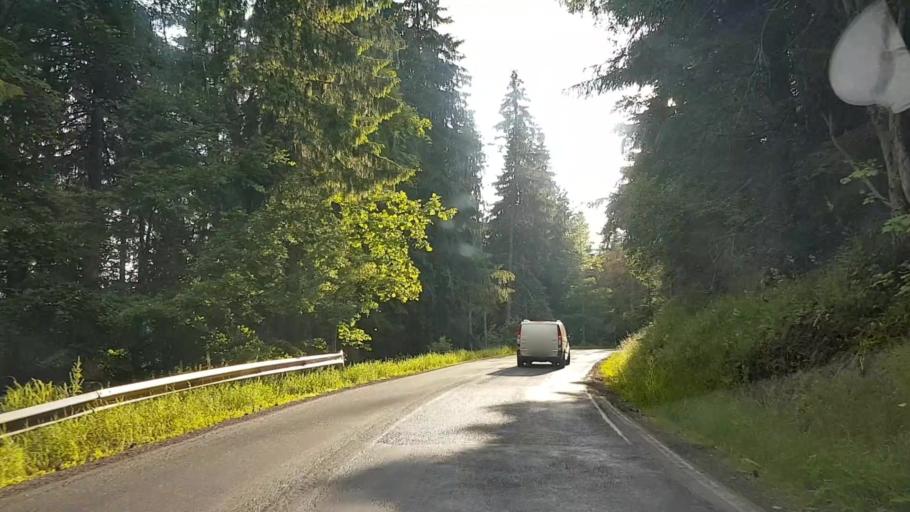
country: RO
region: Harghita
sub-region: Comuna Varsag
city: Varsag
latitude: 46.6629
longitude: 25.3172
